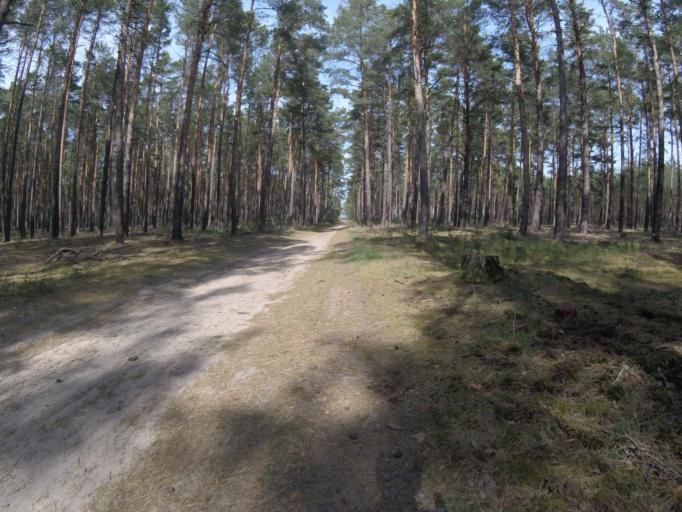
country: DE
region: Brandenburg
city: Bestensee
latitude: 52.2132
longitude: 13.6630
